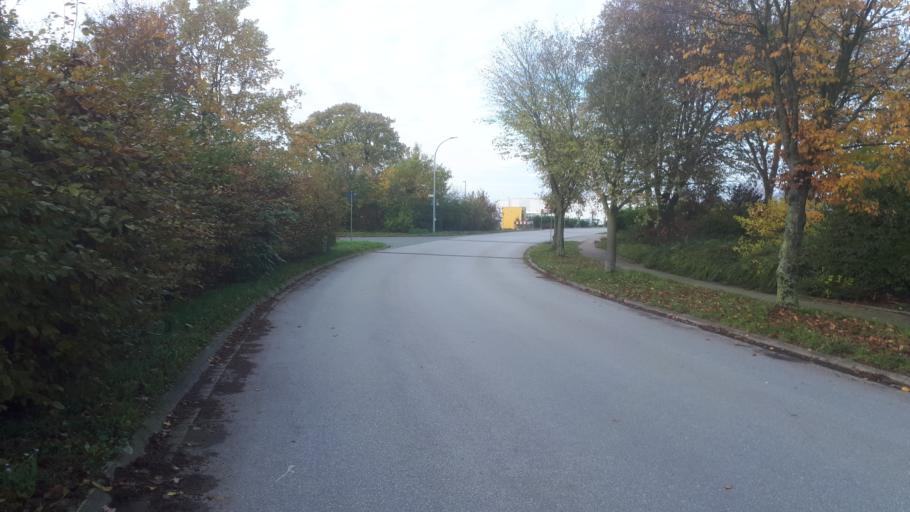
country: DE
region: North Rhine-Westphalia
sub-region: Regierungsbezirk Detmold
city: Huellhorst
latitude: 52.2645
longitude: 8.7081
